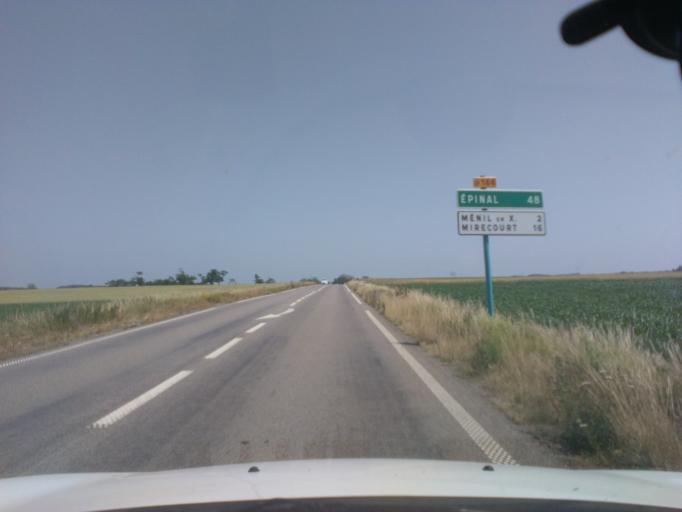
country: FR
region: Lorraine
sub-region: Departement des Vosges
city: Vittel
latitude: 48.3103
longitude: 5.9544
